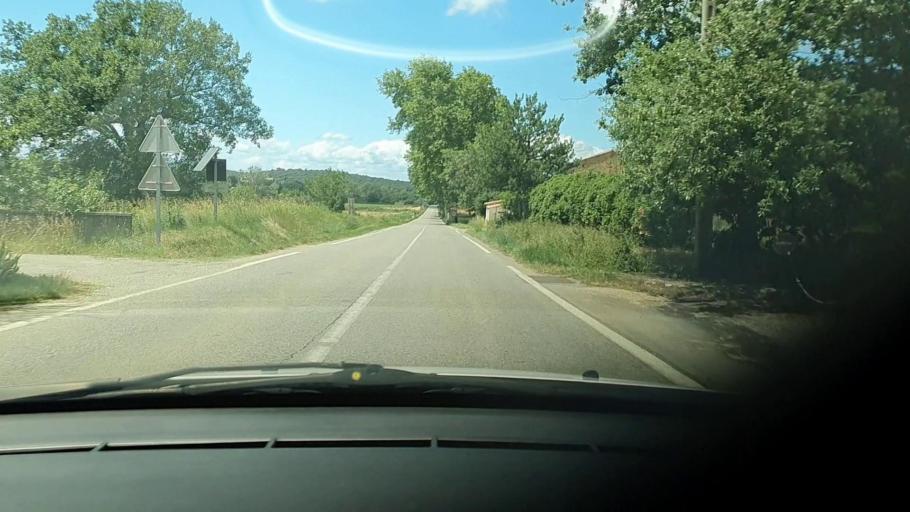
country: FR
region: Languedoc-Roussillon
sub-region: Departement du Gard
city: Saint-Chaptes
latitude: 44.0452
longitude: 4.2980
